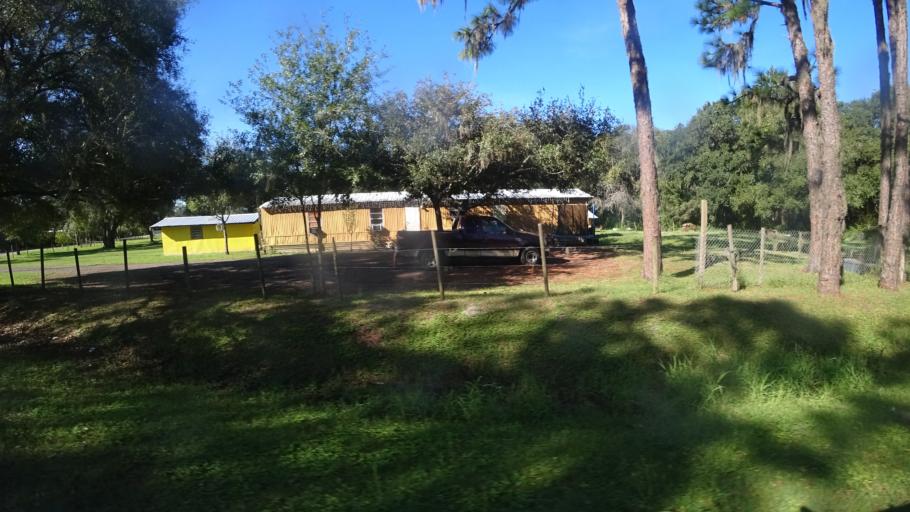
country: US
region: Florida
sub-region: Hillsborough County
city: Sun City Center
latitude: 27.6505
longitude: -82.3606
